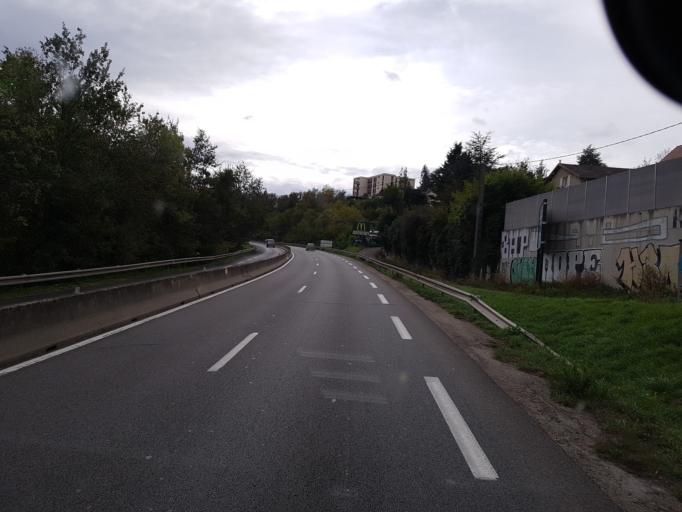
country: FR
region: Rhone-Alpes
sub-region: Departement de la Loire
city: Saint-Genest-Lerpt
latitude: 45.4503
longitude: 4.3370
